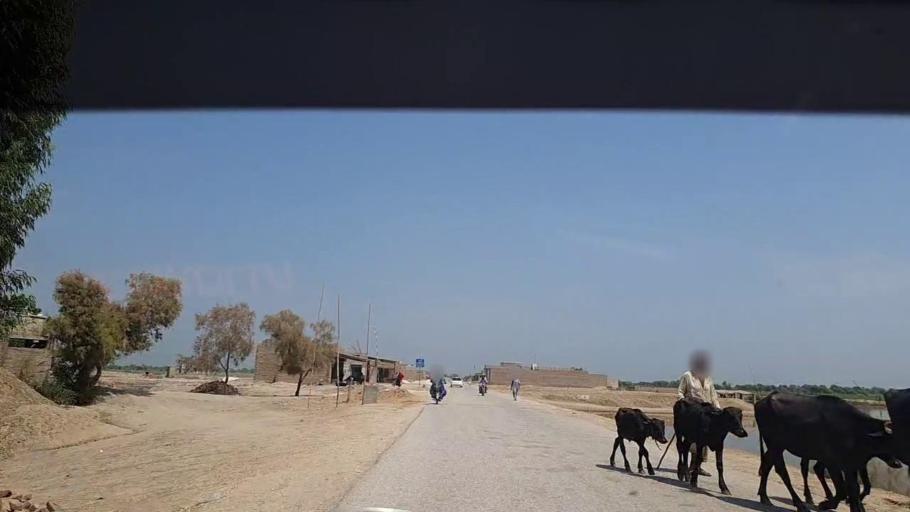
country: PK
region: Sindh
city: Thul
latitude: 28.1223
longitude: 68.8156
